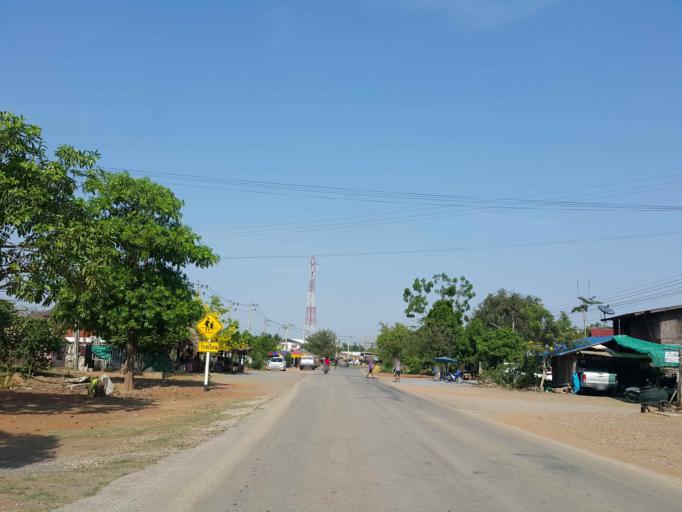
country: TH
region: Sukhothai
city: Thung Saliam
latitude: 17.3267
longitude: 99.6269
